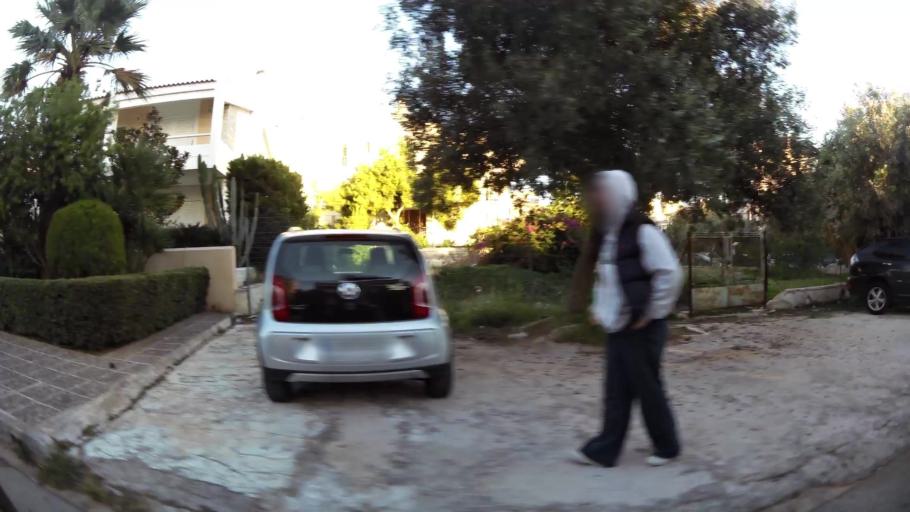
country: GR
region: Attica
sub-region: Nomarchia Athinas
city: Glyfada
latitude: 37.8789
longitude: 23.7530
